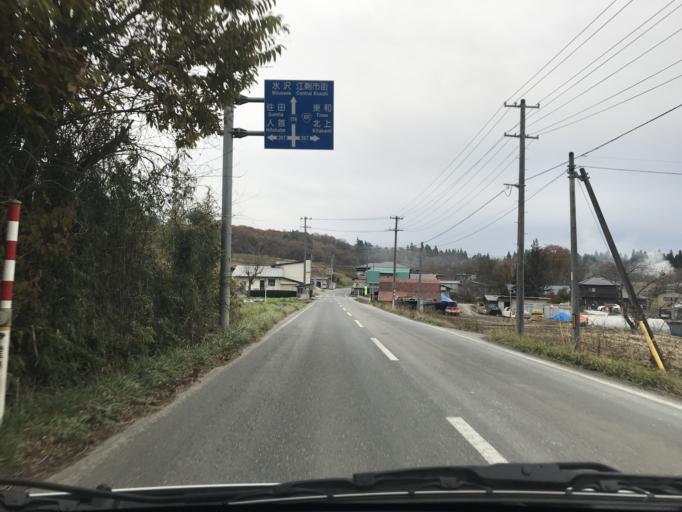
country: JP
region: Iwate
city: Kitakami
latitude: 39.2565
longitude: 141.2667
